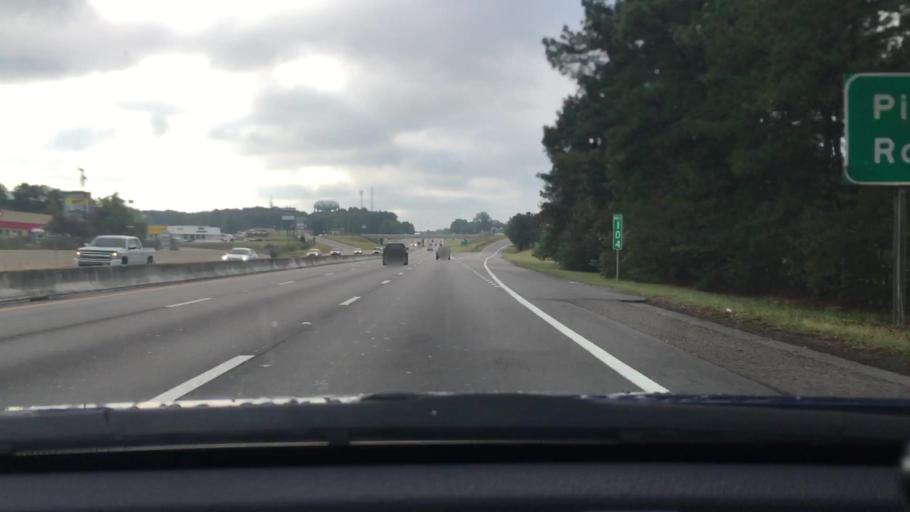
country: US
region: South Carolina
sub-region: Lexington County
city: Seven Oaks
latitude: 34.0713
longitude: -81.1462
